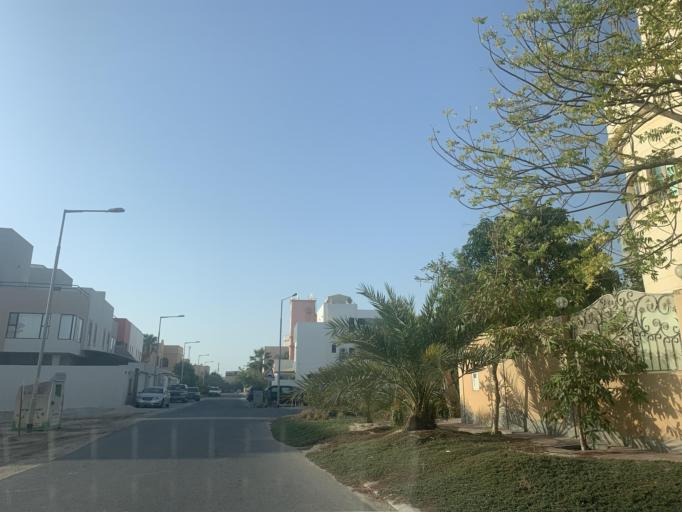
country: BH
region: Manama
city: Jidd Hafs
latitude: 26.2090
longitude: 50.5288
